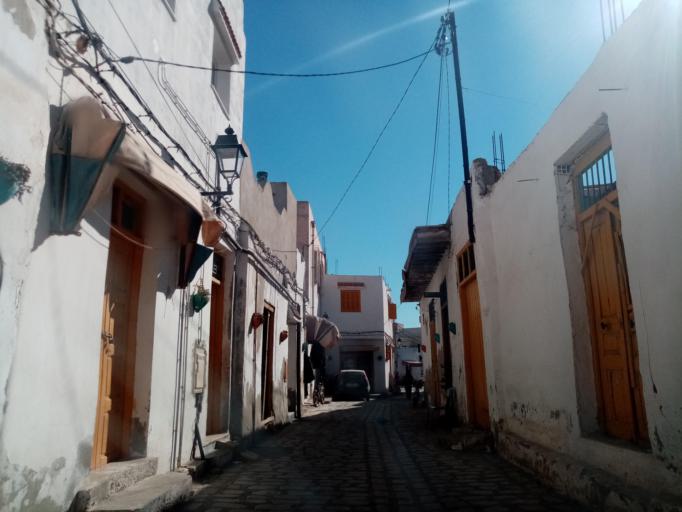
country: TN
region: Qabis
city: Gabes
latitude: 33.8817
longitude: 10.0887
